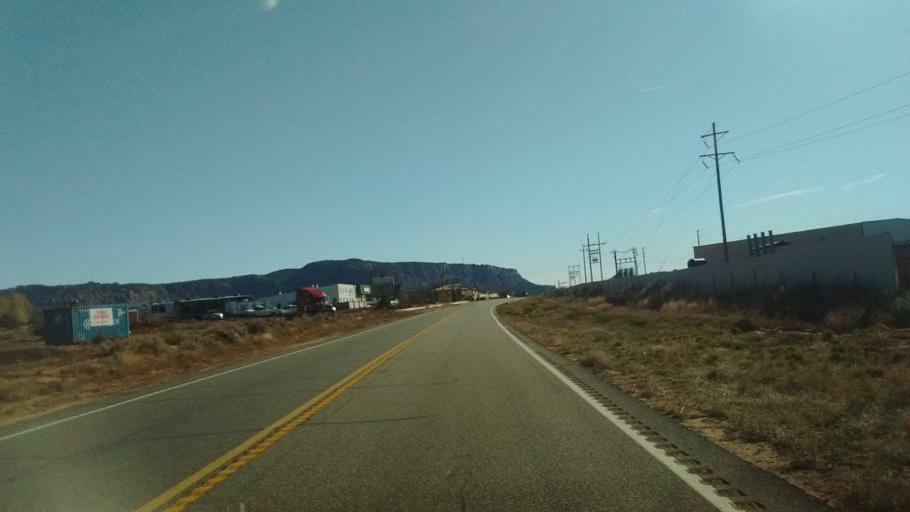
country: US
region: Arizona
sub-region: Mohave County
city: Colorado City
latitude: 37.0048
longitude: -113.0042
